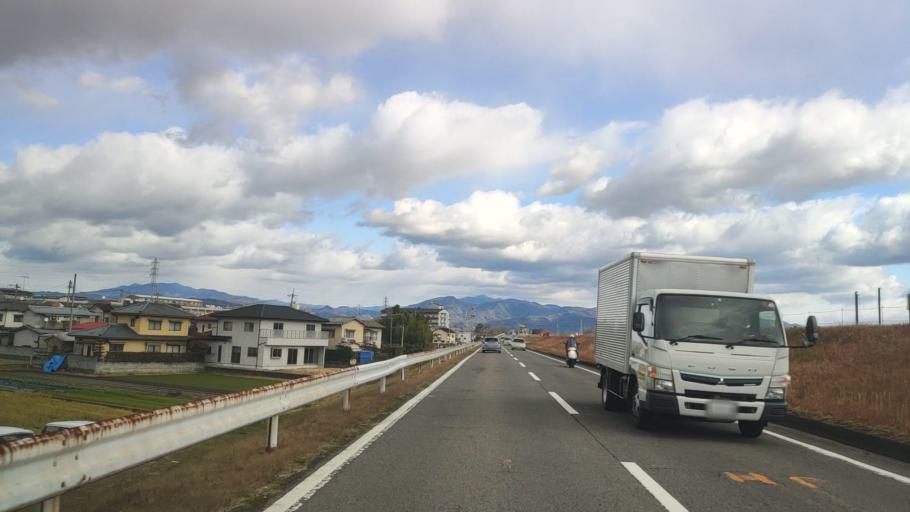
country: JP
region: Ehime
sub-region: Shikoku-chuo Shi
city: Matsuyama
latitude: 33.8123
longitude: 132.7444
